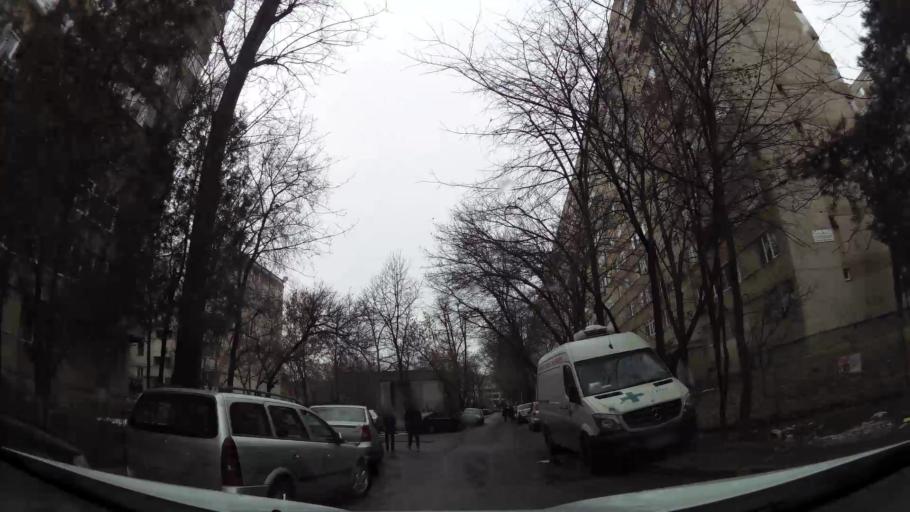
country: RO
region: Ilfov
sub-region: Comuna Chiajna
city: Rosu
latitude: 44.4218
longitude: 26.0195
